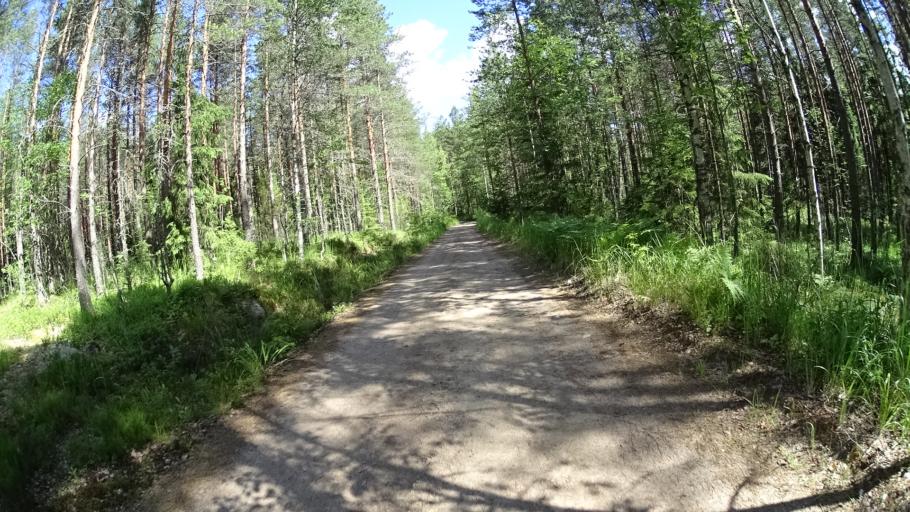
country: FI
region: Uusimaa
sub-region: Helsinki
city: Vihti
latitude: 60.3253
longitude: 24.4595
